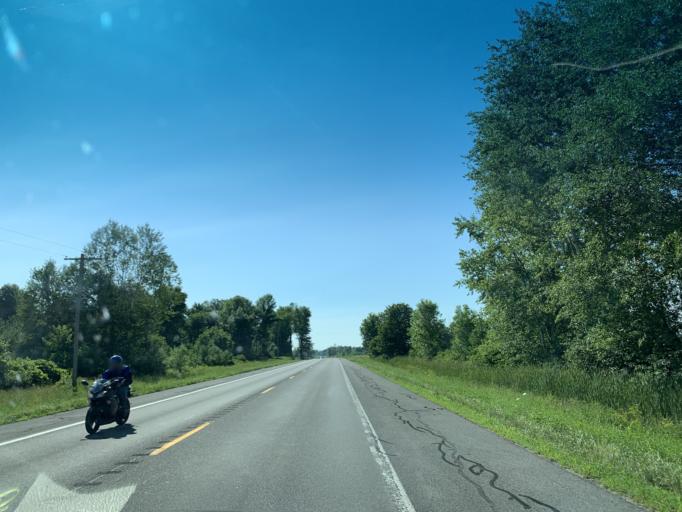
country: US
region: New York
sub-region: Madison County
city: Oneida
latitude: 43.1403
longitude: -75.6297
